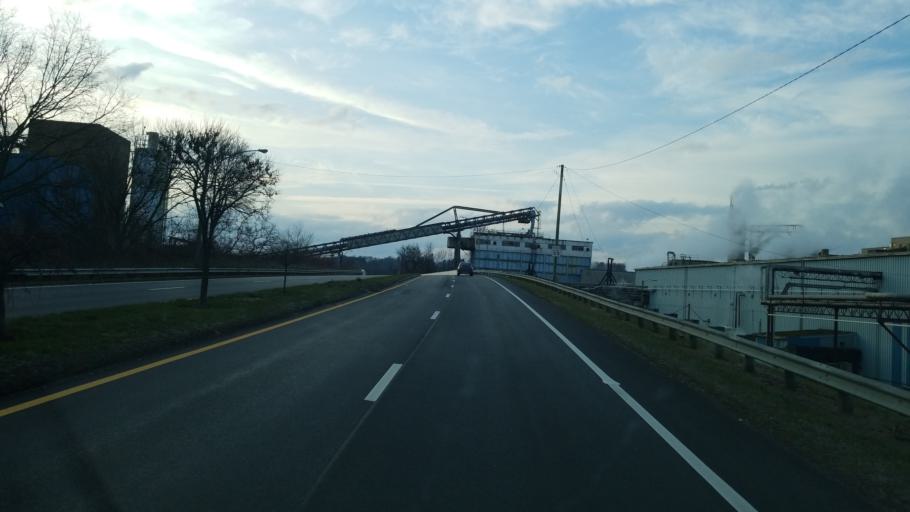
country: US
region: Ohio
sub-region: Ross County
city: Chillicothe
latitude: 39.3256
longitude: -82.9722
